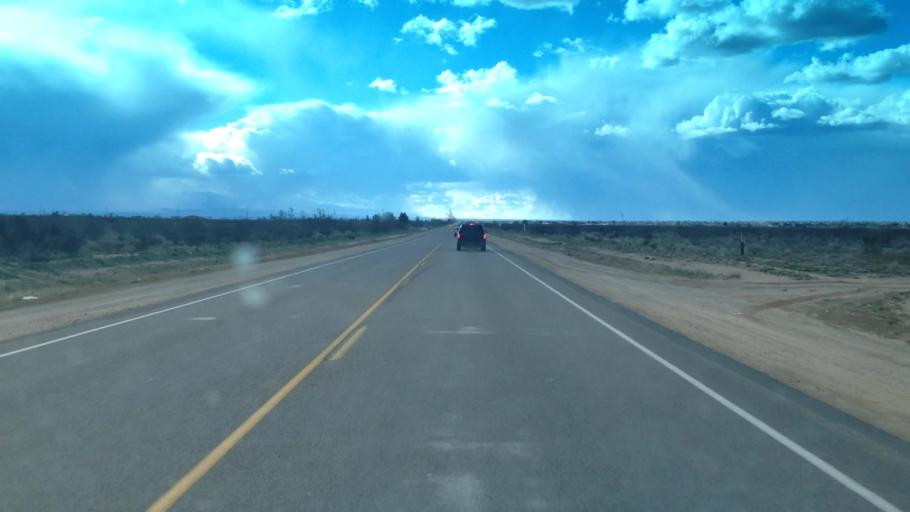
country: US
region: California
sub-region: San Bernardino County
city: Apple Valley
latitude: 34.4720
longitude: -117.1334
